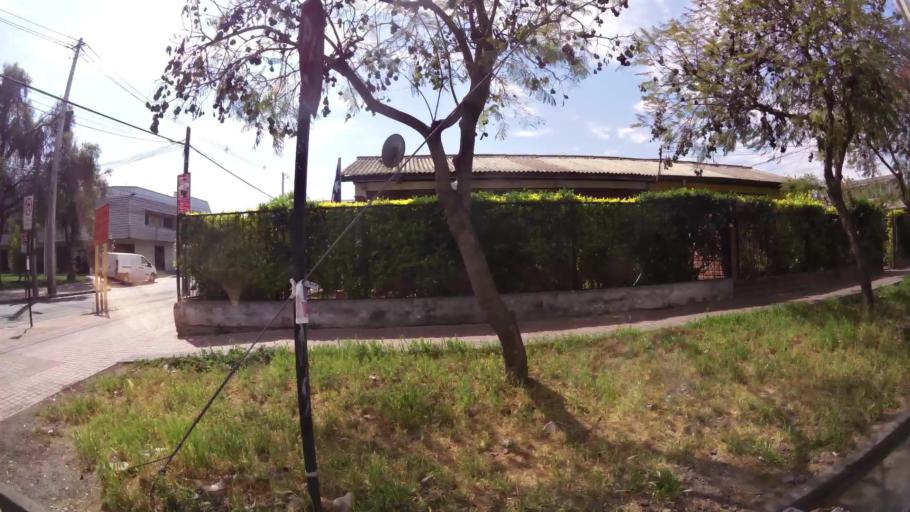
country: CL
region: Santiago Metropolitan
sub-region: Provincia de Talagante
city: Talagante
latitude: -33.6627
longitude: -70.9226
